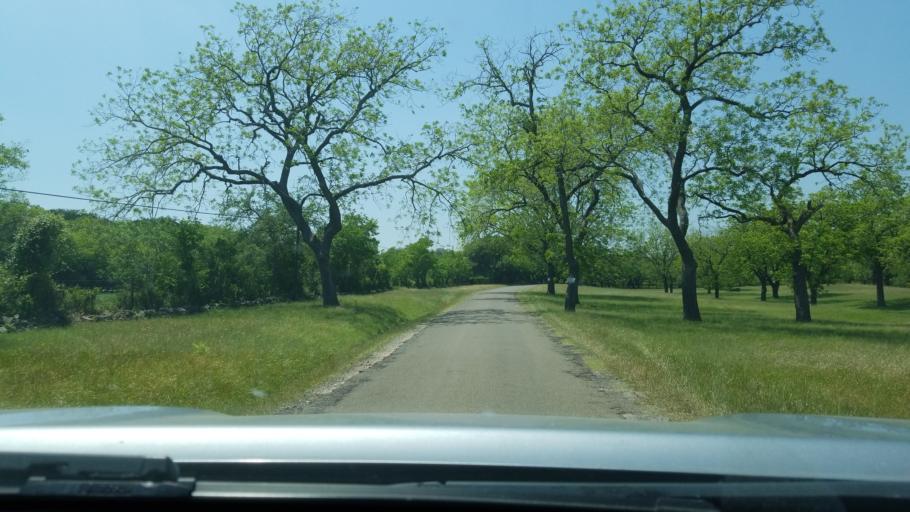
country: US
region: Texas
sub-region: Blanco County
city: Blanco
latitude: 30.0044
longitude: -98.4301
